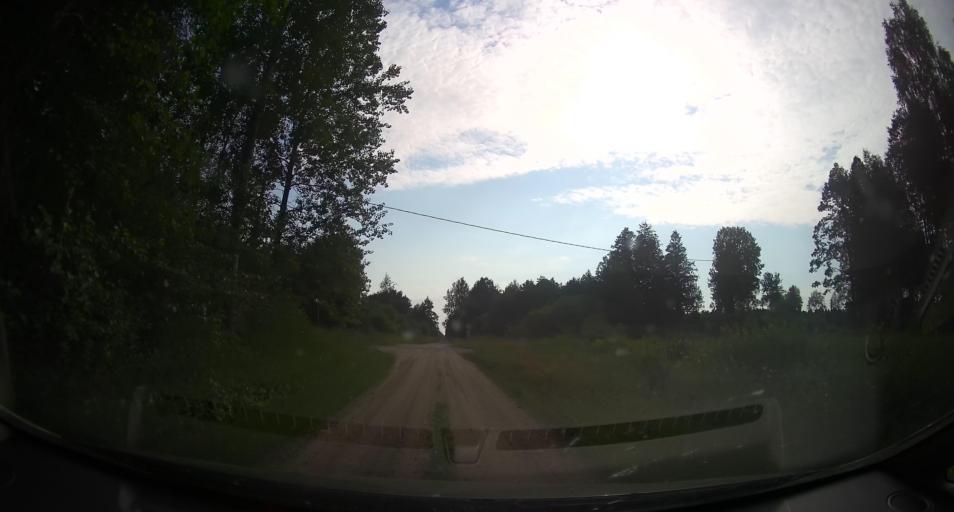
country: EE
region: Laeaene
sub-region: Lihula vald
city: Lihula
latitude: 58.6470
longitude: 23.7829
